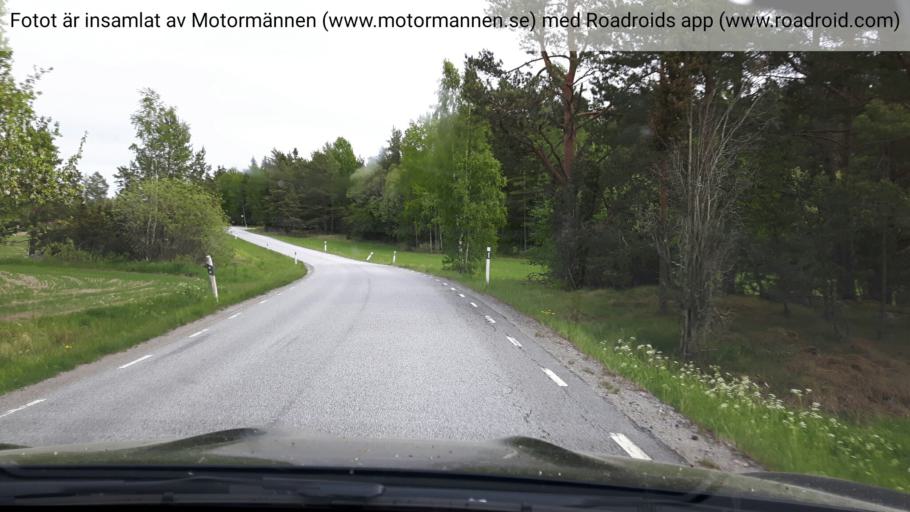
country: SE
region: Stockholm
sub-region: Norrtalje Kommun
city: Bjorko
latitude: 59.6663
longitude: 18.8580
